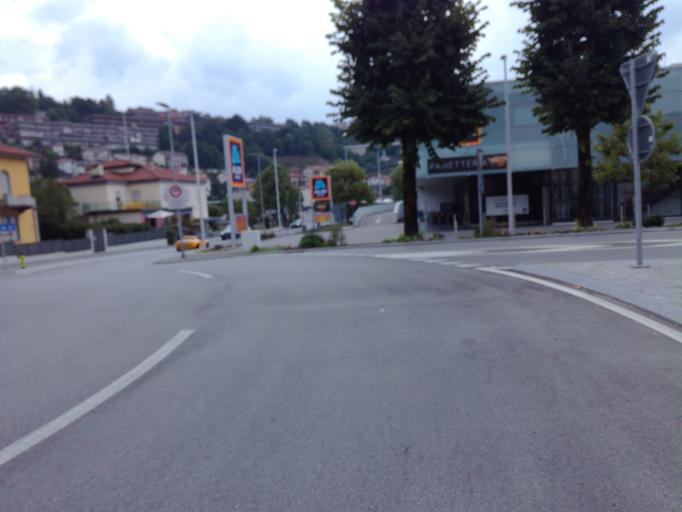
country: CH
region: Ticino
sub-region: Mendrisio District
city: Chiasso
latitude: 45.8365
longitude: 9.0346
